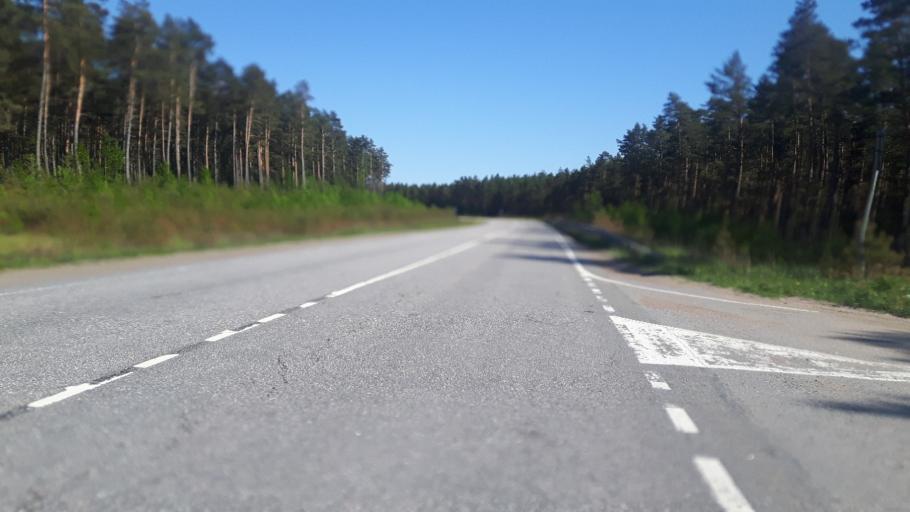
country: RU
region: Leningrad
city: Sosnovyy Bor
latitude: 60.1872
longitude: 29.0243
